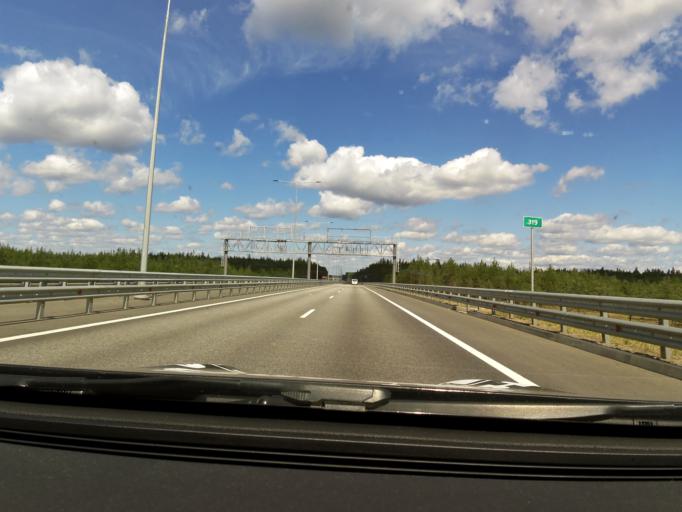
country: RU
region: Tverskaya
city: Krasnomayskiy
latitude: 57.6087
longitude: 34.2483
